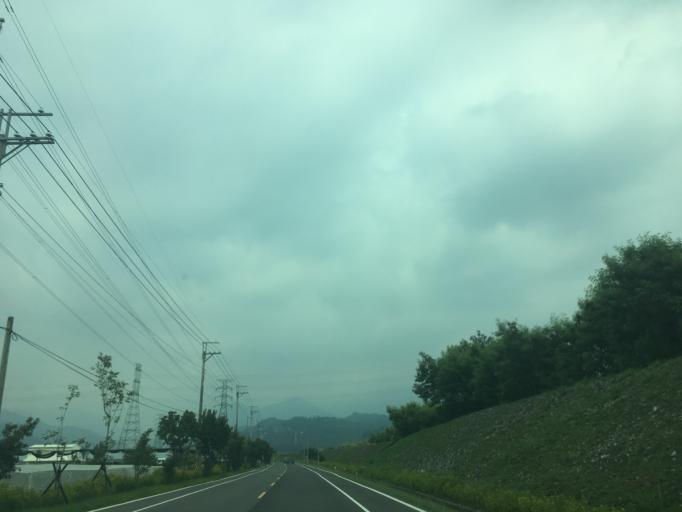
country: TW
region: Taiwan
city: Fengyuan
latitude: 24.2896
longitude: 120.8477
